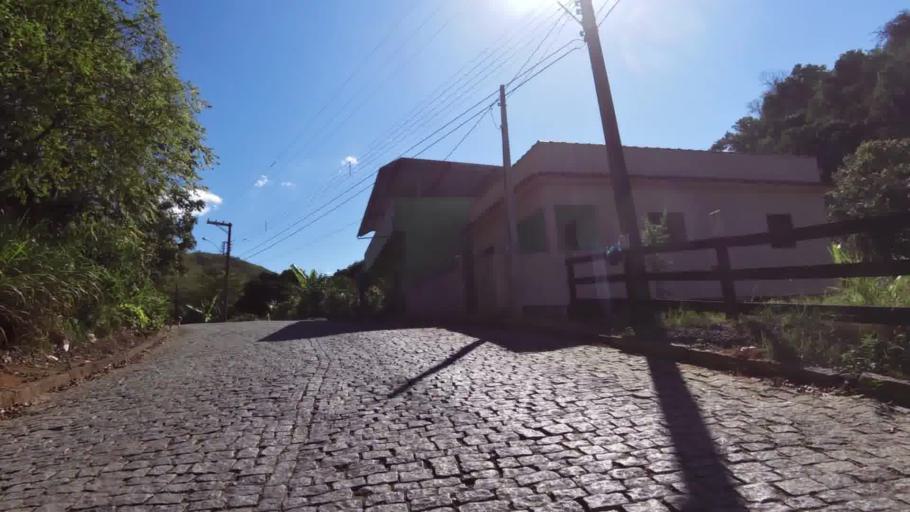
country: BR
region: Espirito Santo
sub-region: Rio Novo Do Sul
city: Rio Novo do Sul
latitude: -20.8583
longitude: -40.9317
